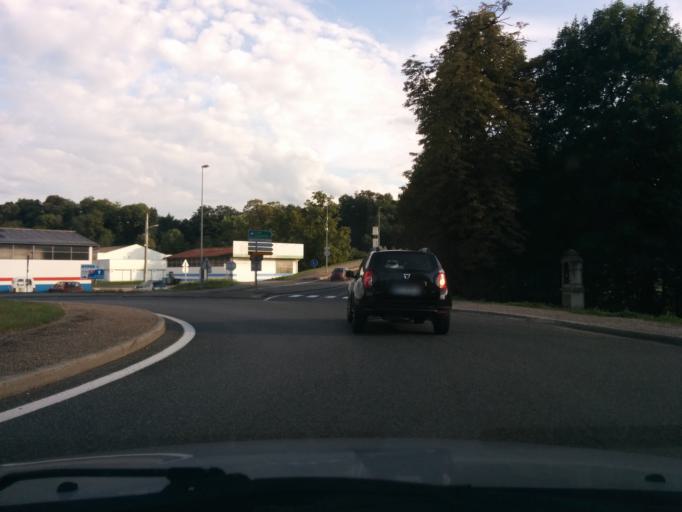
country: FR
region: Rhone-Alpes
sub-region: Departement de la Savoie
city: Le Pont-de-Beauvoisin
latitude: 45.5315
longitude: 5.6810
